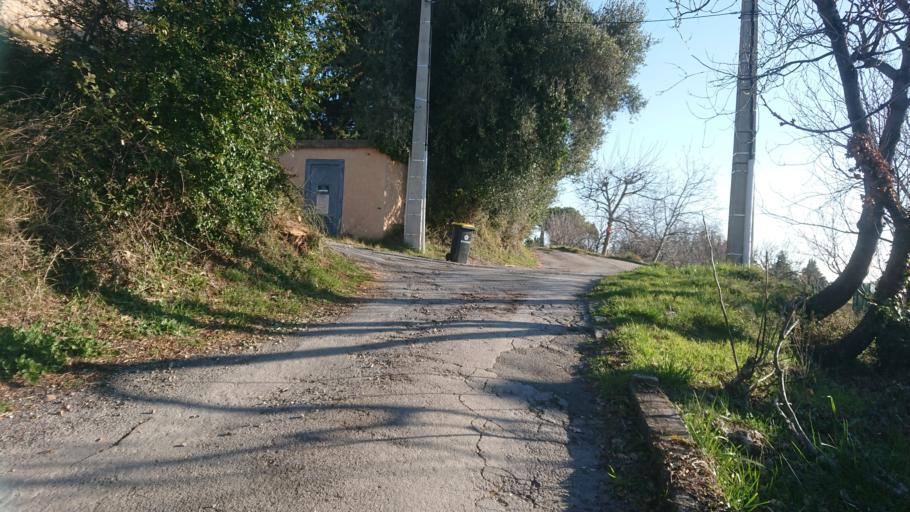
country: FR
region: Provence-Alpes-Cote d'Azur
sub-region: Departement des Alpes-Maritimes
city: Opio
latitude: 43.6843
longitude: 6.9710
